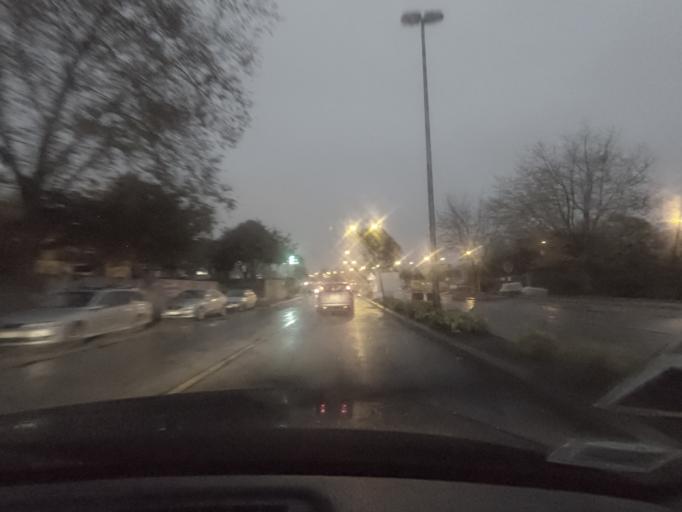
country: PT
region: Porto
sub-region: Matosinhos
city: Senhora da Hora
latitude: 41.1833
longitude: -8.6607
